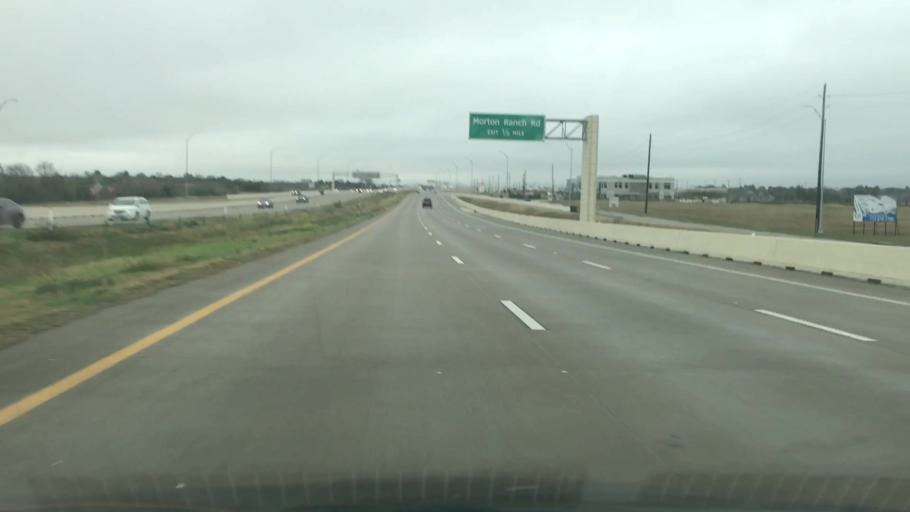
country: US
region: Texas
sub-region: Harris County
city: Katy
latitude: 29.8041
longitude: -95.7751
